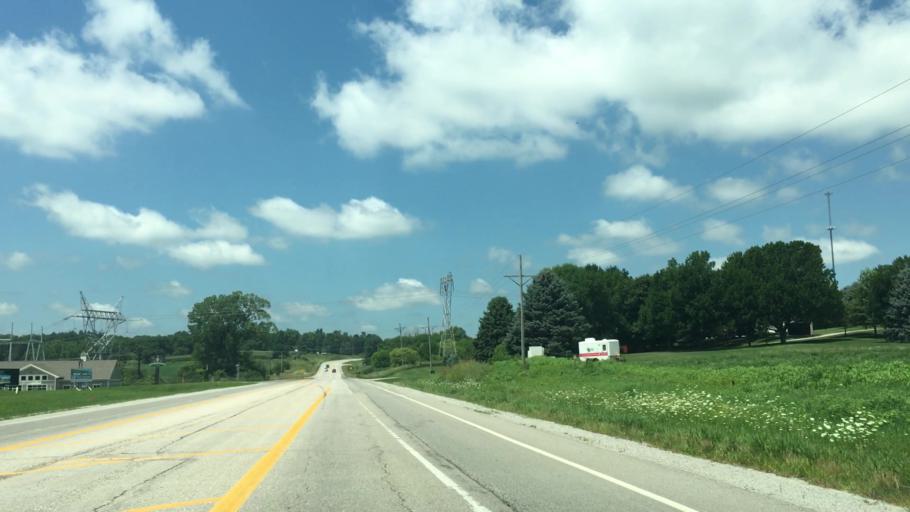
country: US
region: Iowa
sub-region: Johnson County
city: Tiffin
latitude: 41.7084
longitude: -91.6786
